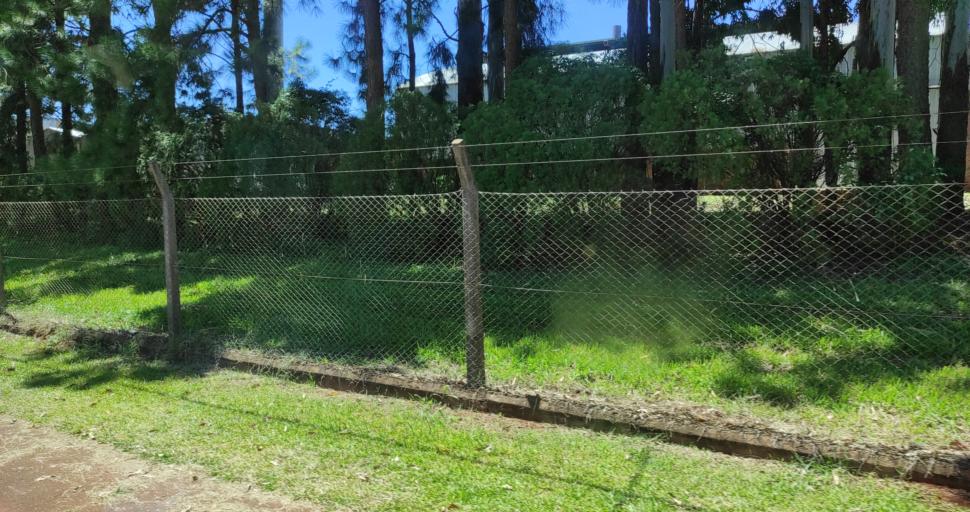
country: AR
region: Misiones
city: Dos de Mayo
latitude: -27.0062
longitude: -54.4789
